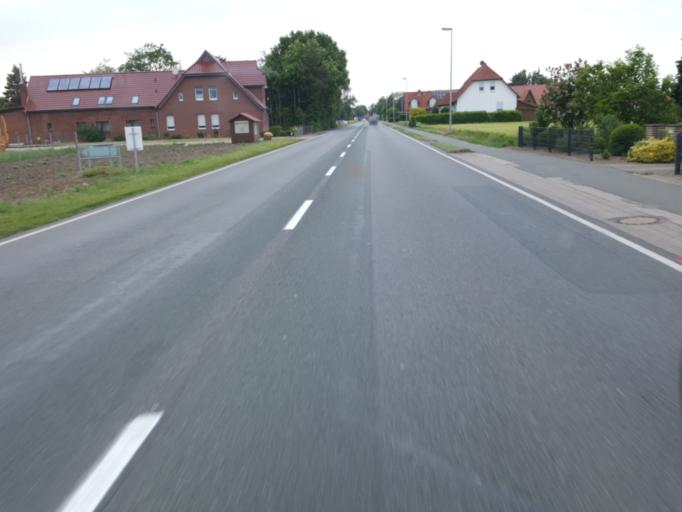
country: DE
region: Lower Saxony
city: Leese
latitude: 52.4952
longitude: 9.1212
